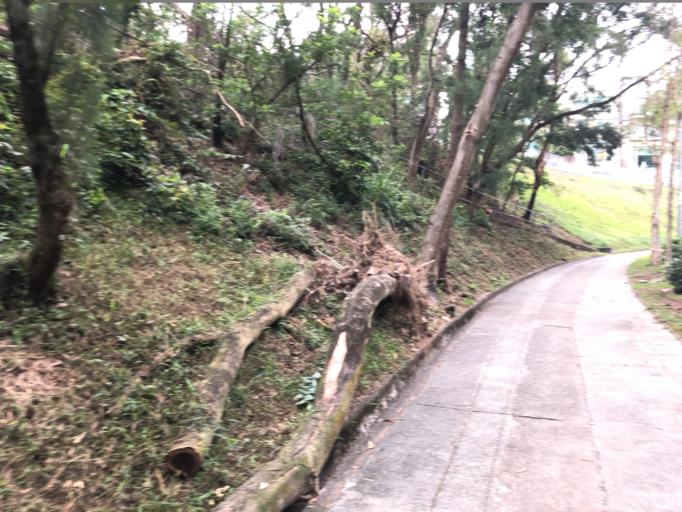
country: HK
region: Tai Po
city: Tai Po
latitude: 22.4648
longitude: 114.1930
